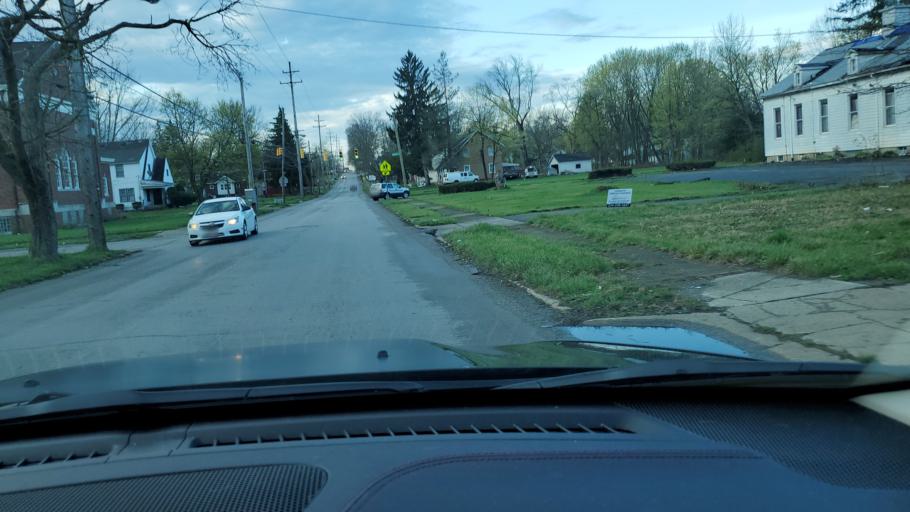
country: US
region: Ohio
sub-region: Mahoning County
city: Youngstown
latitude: 41.0676
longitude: -80.6640
